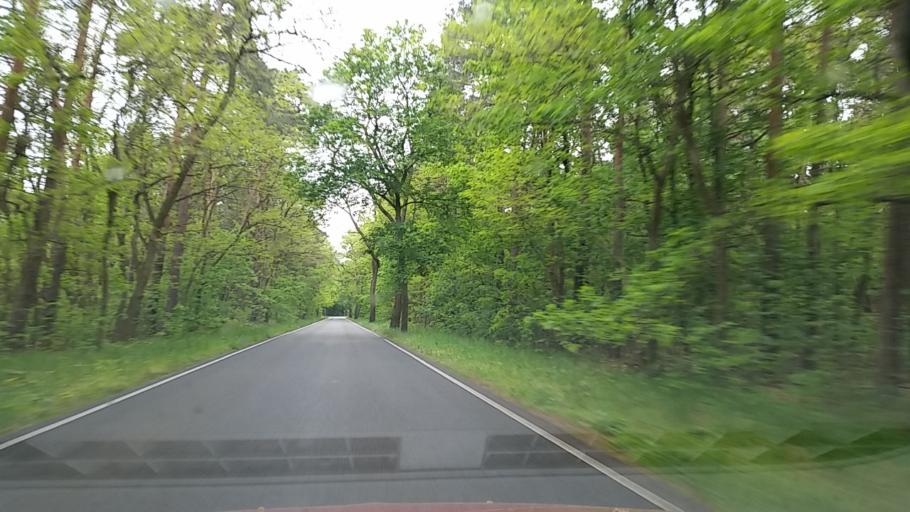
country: DE
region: Brandenburg
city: Diensdorf-Radlow
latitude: 52.2684
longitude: 14.0381
